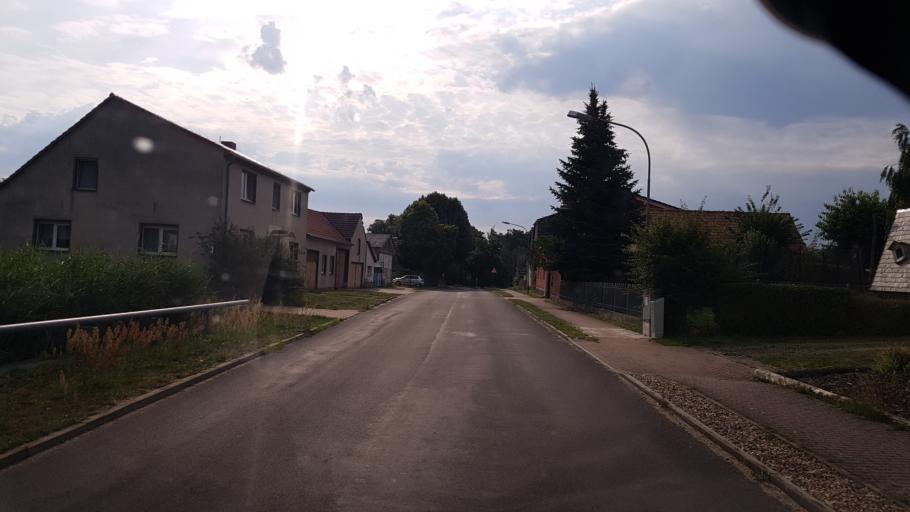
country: DE
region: Brandenburg
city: Dahme
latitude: 51.9501
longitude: 13.4741
